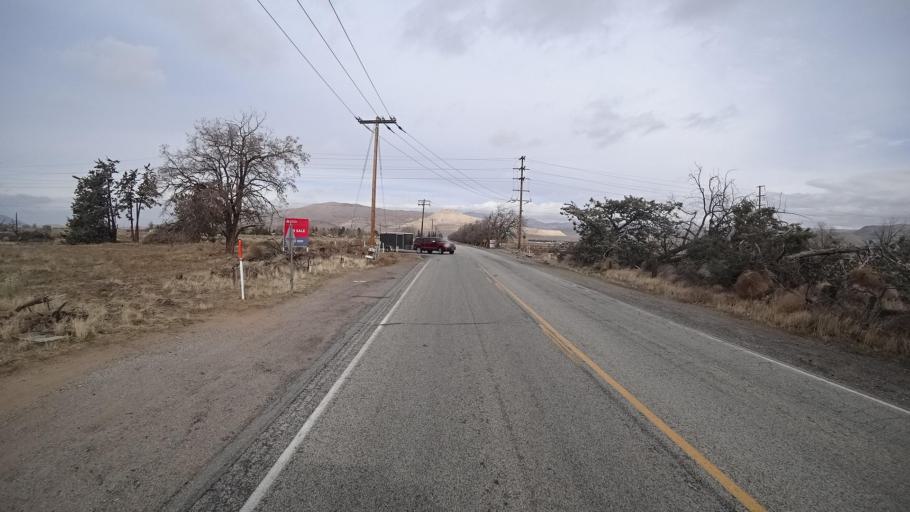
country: US
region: California
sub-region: Kern County
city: Tehachapi
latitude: 35.1092
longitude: -118.3967
